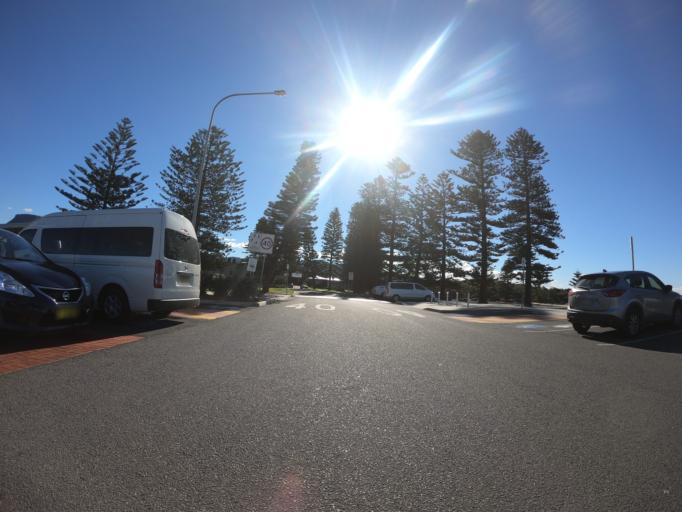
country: AU
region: New South Wales
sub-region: Wollongong
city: Fairy Meadow
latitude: -34.4103
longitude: 150.9006
